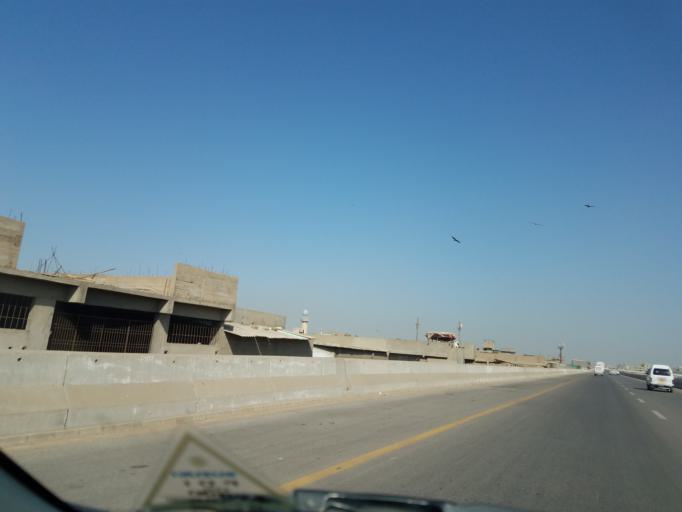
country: PK
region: Sindh
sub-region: Karachi District
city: Karachi
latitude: 24.8821
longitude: 66.9985
